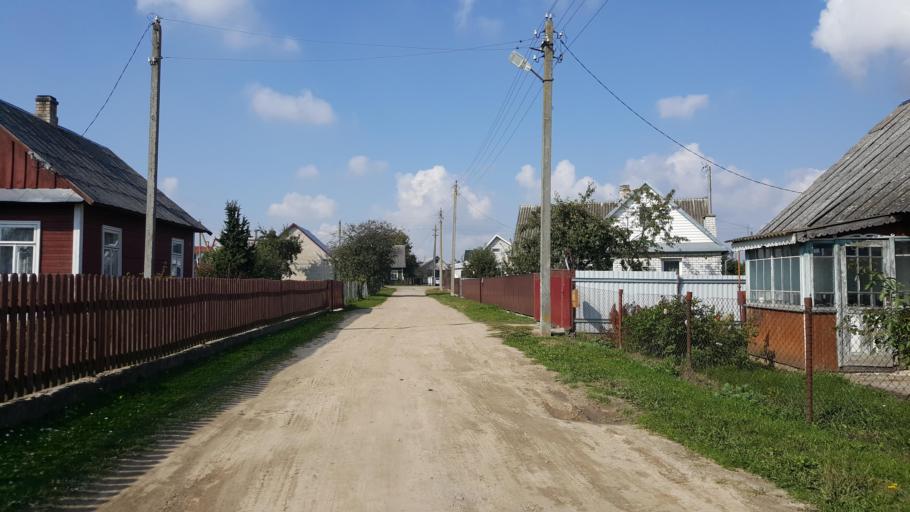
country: BY
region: Brest
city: Kamyanyets
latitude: 52.4048
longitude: 23.7980
